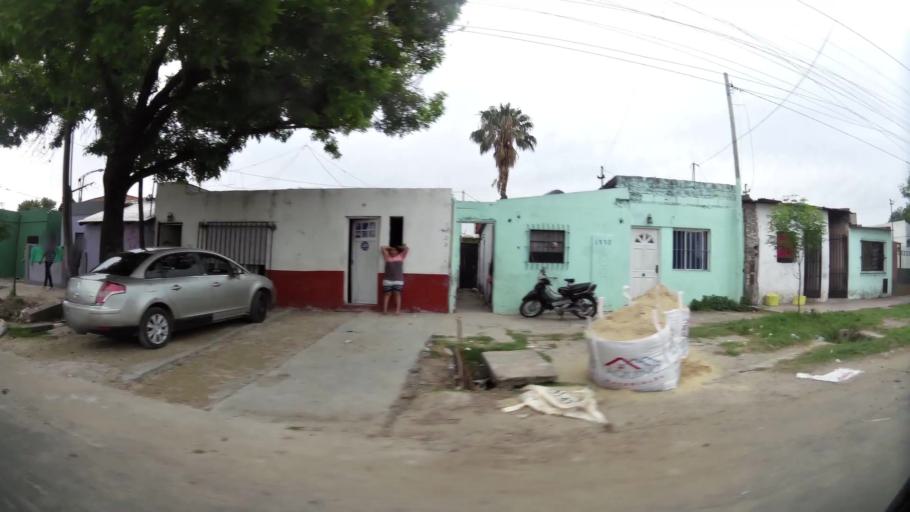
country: AR
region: Santa Fe
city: Granadero Baigorria
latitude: -32.8993
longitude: -60.7056
